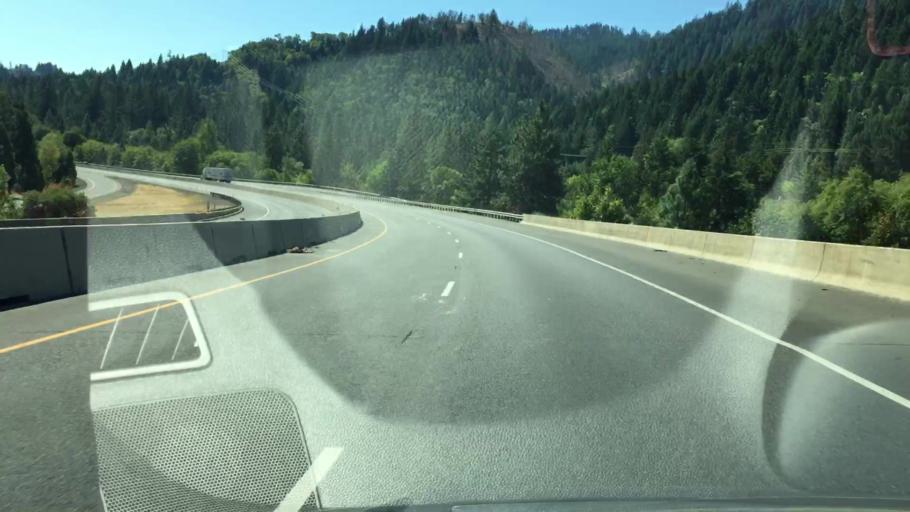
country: US
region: Oregon
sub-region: Josephine County
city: Merlin
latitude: 42.6905
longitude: -123.3939
